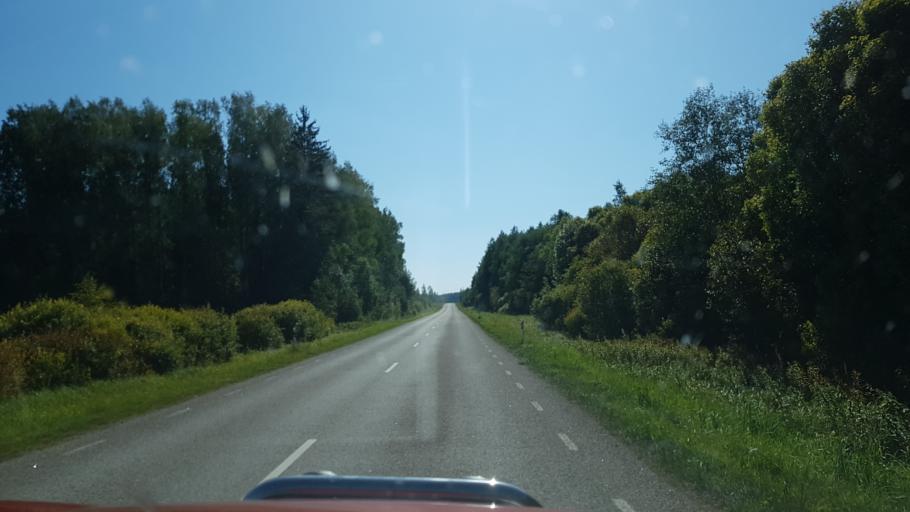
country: EE
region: Polvamaa
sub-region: Polva linn
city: Polva
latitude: 58.2319
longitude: 27.2212
